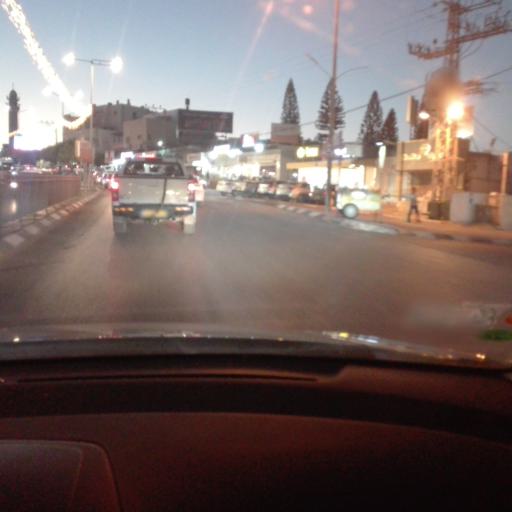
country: PS
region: West Bank
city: Nazlat `Isa
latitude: 32.4199
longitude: 35.0449
